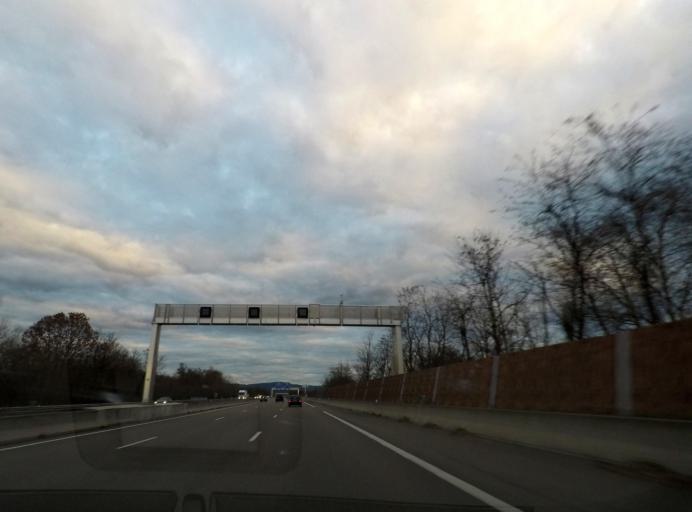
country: FR
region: Rhone-Alpes
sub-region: Departement de l'Ain
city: Saint-Martin-du-Mont
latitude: 46.0775
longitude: 5.3005
